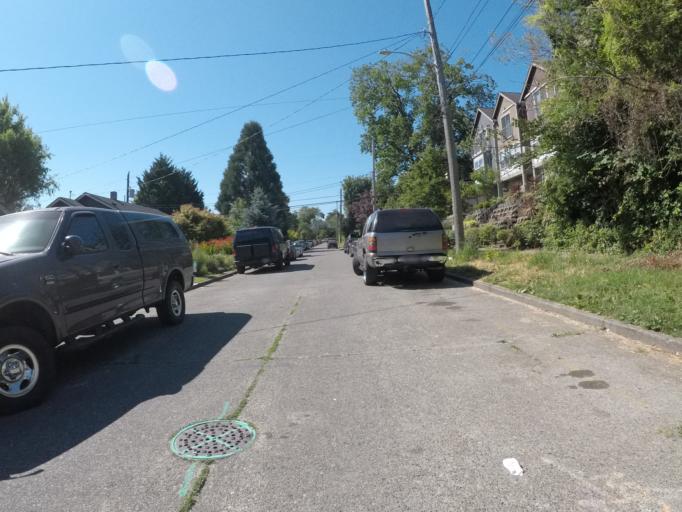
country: US
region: Washington
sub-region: King County
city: Seattle
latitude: 47.6194
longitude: -122.2986
